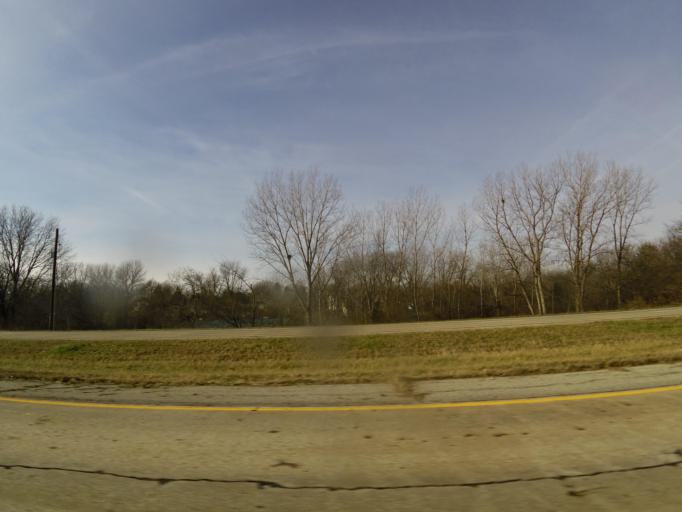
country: US
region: Illinois
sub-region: De Witt County
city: Clinton
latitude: 40.1007
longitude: -88.9653
